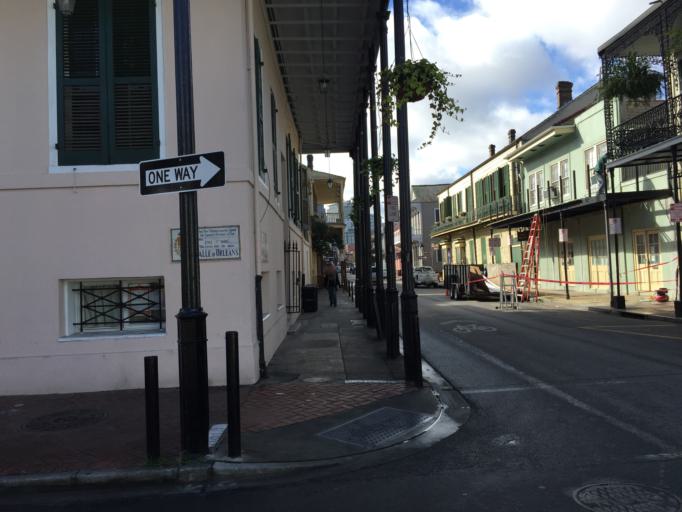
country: US
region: Louisiana
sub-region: Orleans Parish
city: New Orleans
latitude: 29.9597
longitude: -90.0661
